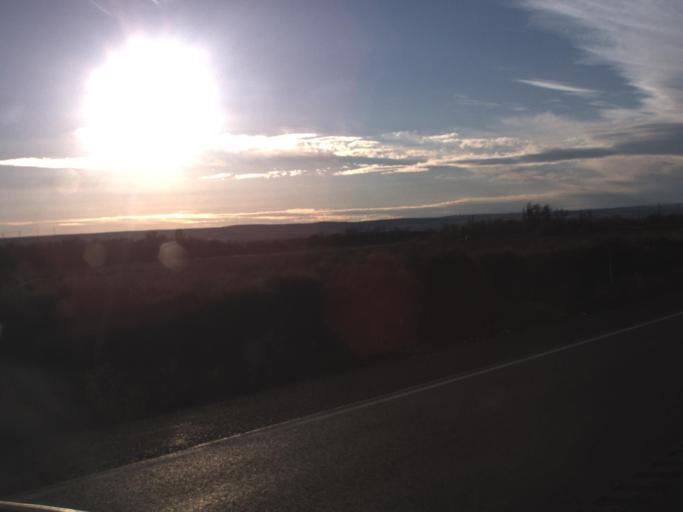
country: US
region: Washington
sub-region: Walla Walla County
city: Garrett
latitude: 46.0514
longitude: -118.5398
